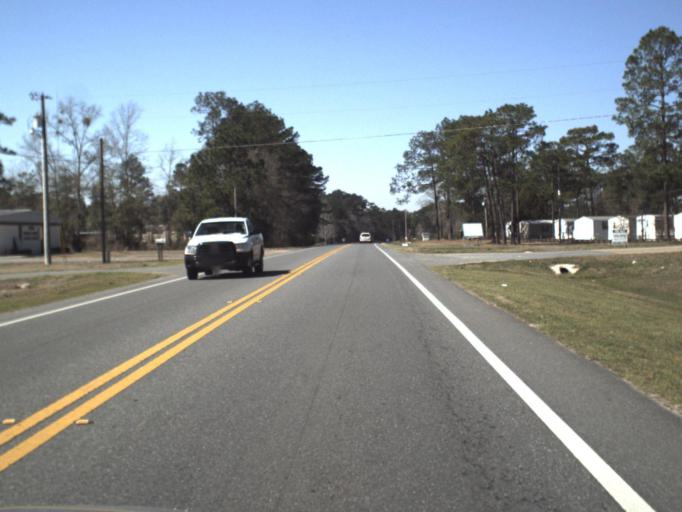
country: US
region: Florida
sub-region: Jackson County
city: Marianna
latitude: 30.7465
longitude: -85.1755
